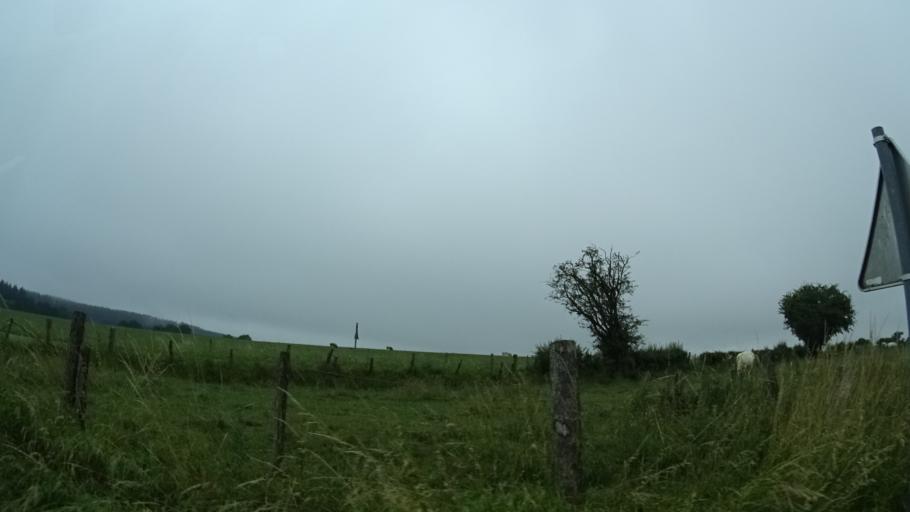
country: BE
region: Wallonia
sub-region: Province du Luxembourg
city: Leglise
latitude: 49.7792
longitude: 5.5642
